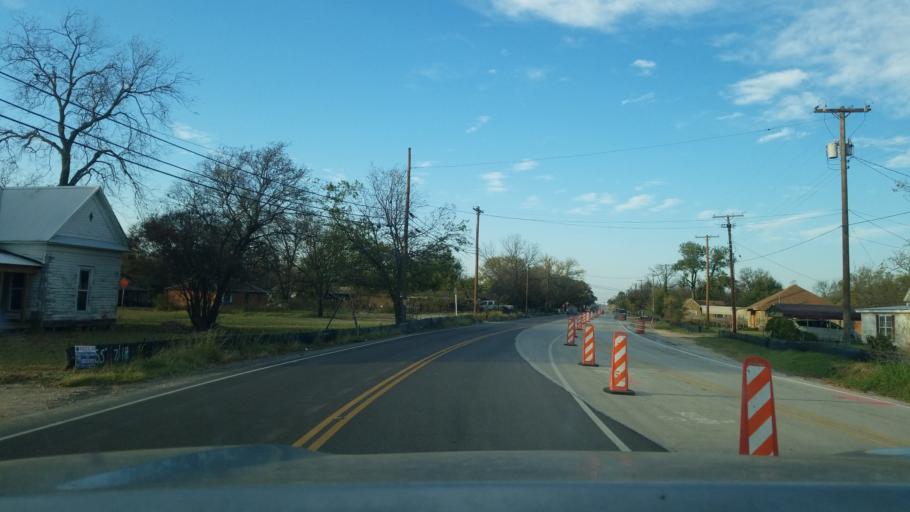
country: US
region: Texas
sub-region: Brown County
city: Lake Brownwood
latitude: 32.0999
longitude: -98.9643
